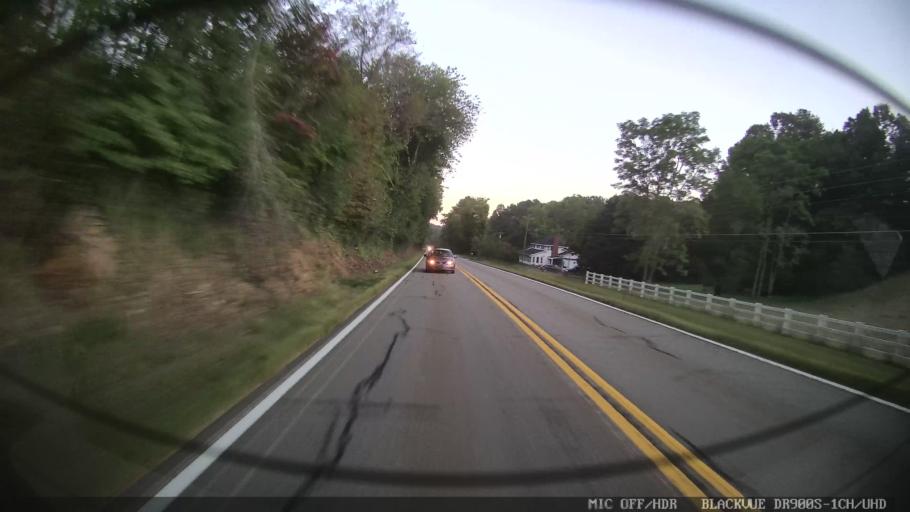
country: US
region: Georgia
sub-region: Gilmer County
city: Ellijay
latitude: 34.7257
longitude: -84.5078
